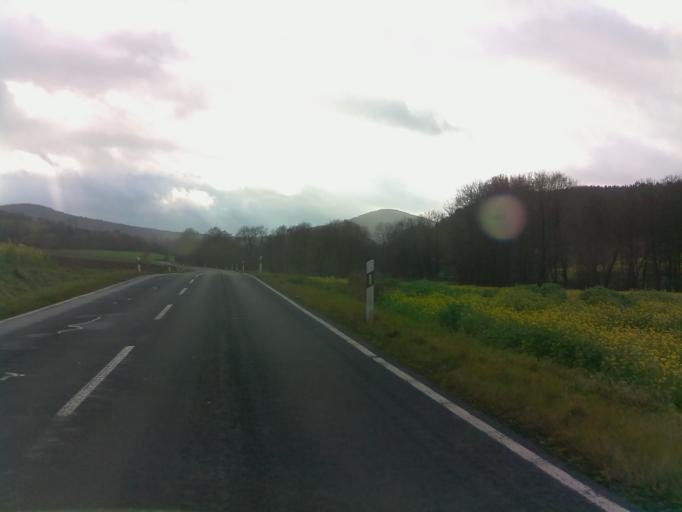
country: DE
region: Hesse
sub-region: Regierungsbezirk Kassel
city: Rasdorf
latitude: 50.7515
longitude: 9.8816
